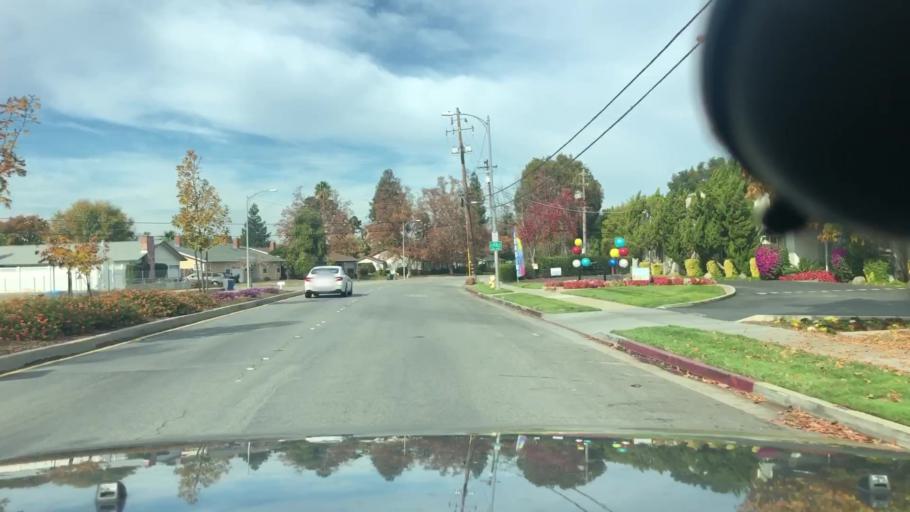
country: US
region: California
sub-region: Santa Clara County
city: Cupertino
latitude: 37.3193
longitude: -122.0137
